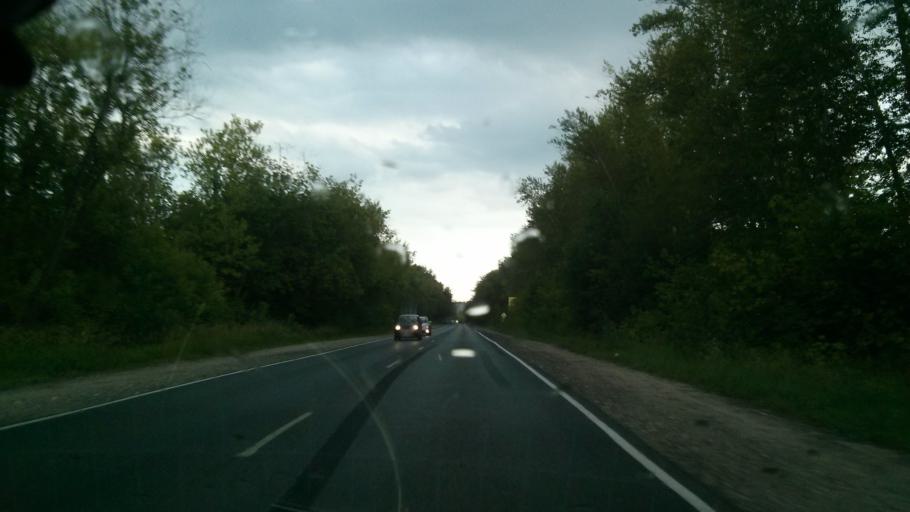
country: RU
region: Vladimir
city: Murom
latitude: 55.6131
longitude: 42.0260
